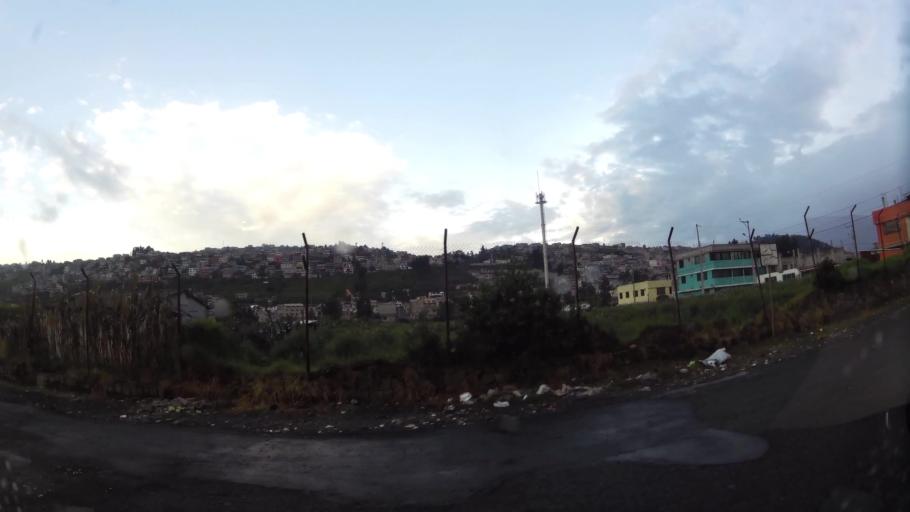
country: EC
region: Pichincha
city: Quito
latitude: -0.3004
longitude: -78.5385
